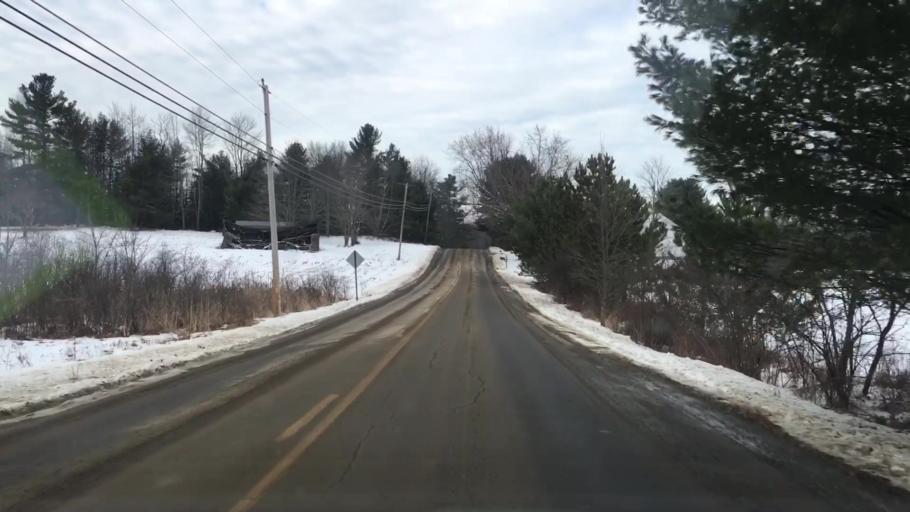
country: US
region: Maine
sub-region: Lincoln County
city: Whitefield
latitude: 44.2299
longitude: -69.6142
